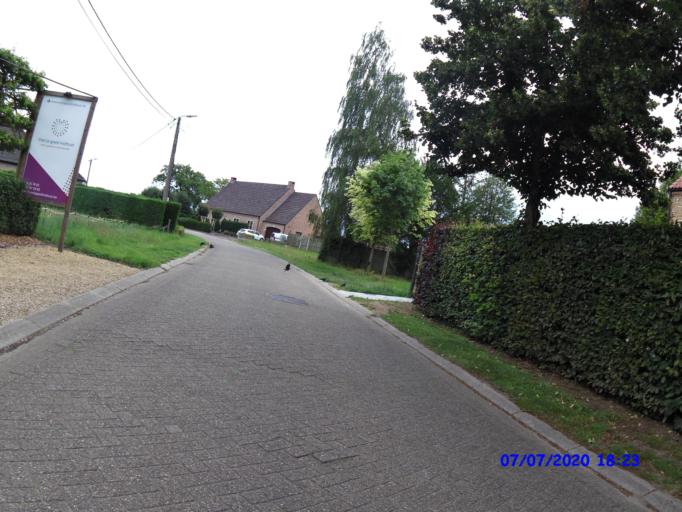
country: BE
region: Flanders
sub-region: Provincie Antwerpen
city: Olen
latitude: 51.1167
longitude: 4.8216
